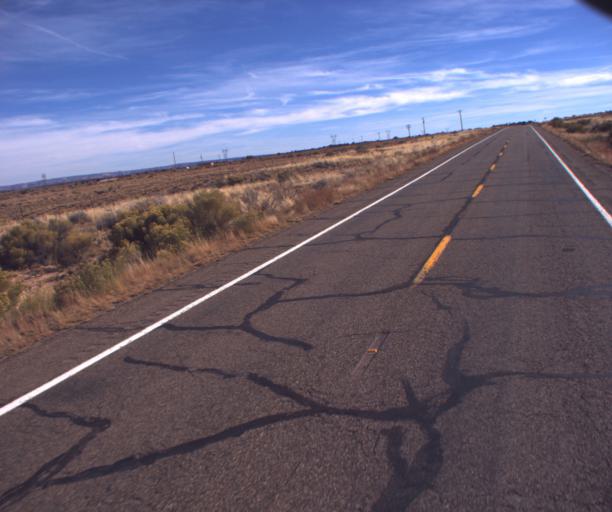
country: US
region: Arizona
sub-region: Coconino County
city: Kaibito
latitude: 36.6165
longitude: -110.9487
